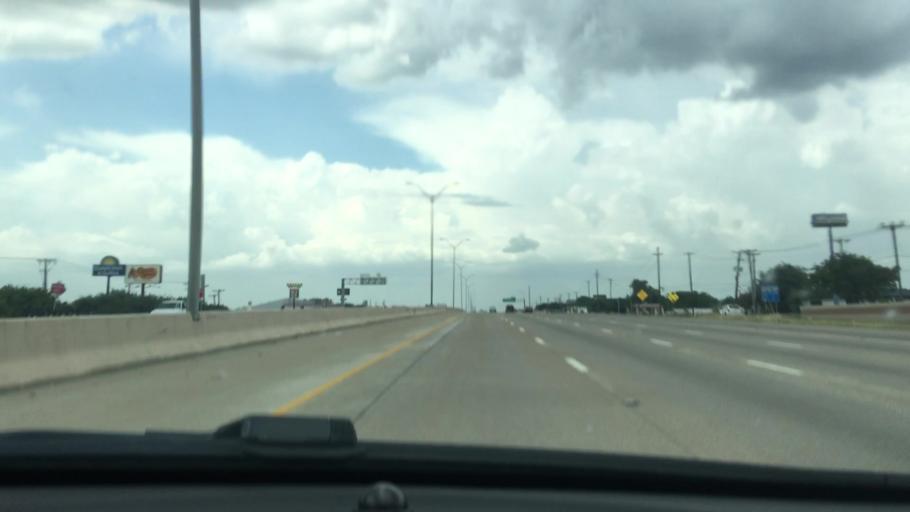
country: US
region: Texas
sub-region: Dallas County
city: DeSoto
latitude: 32.6160
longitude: -96.8230
